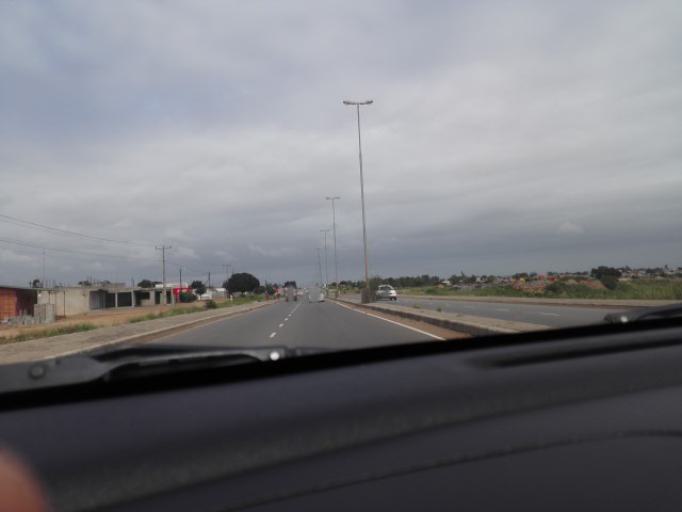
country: MZ
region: Maputo City
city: Maputo
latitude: -25.8281
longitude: 32.6073
